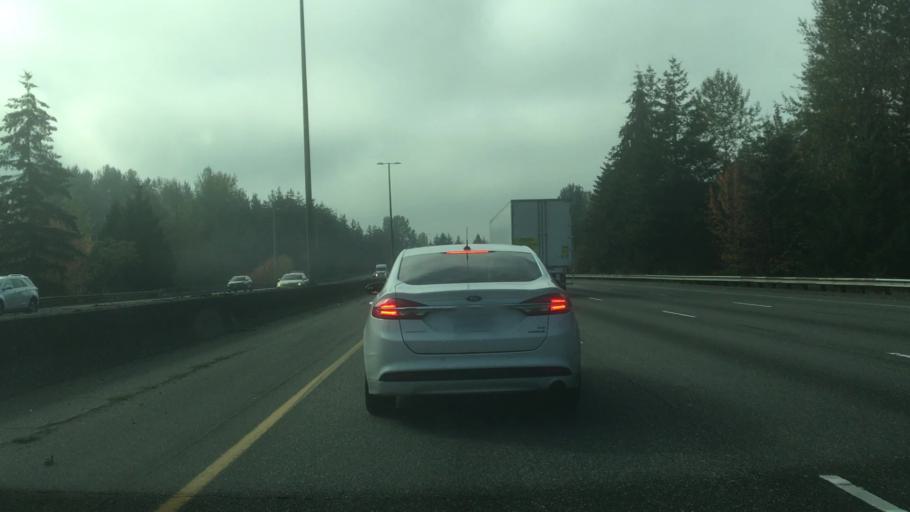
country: US
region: Washington
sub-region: Thurston County
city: Lacey
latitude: 47.0422
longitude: -122.8500
